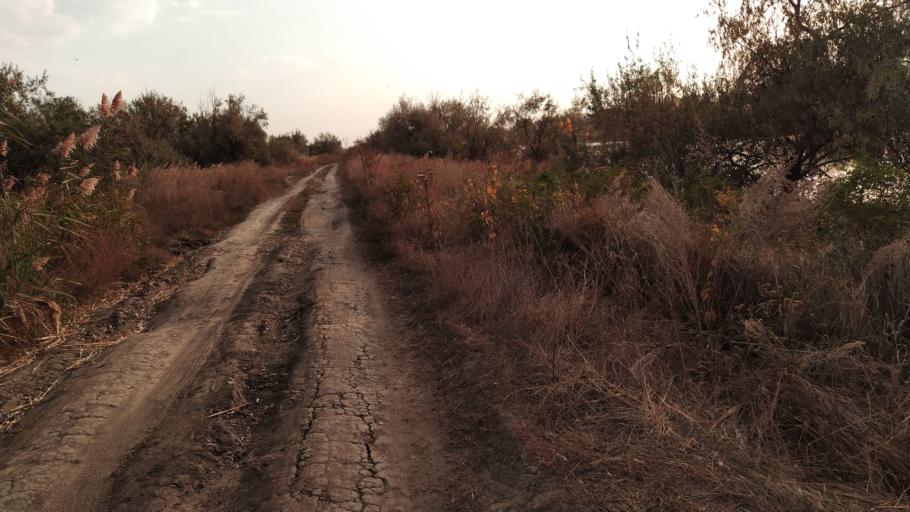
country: RU
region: Rostov
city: Kuleshovka
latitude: 47.1207
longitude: 39.6034
